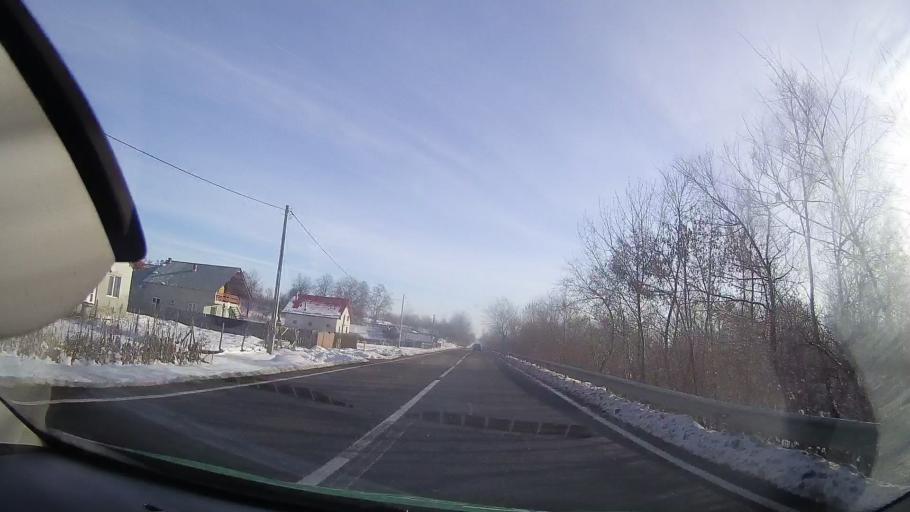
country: RO
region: Neamt
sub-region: Comuna Ghindaoani
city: Ghindaoani
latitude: 47.0718
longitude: 26.3626
